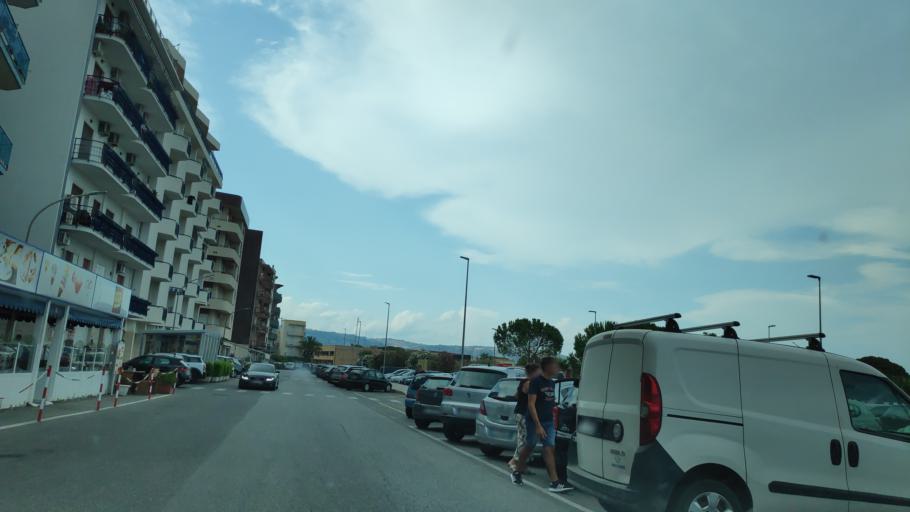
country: IT
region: Calabria
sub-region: Provincia di Catanzaro
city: Soverato Marina
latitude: 38.6863
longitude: 16.5548
